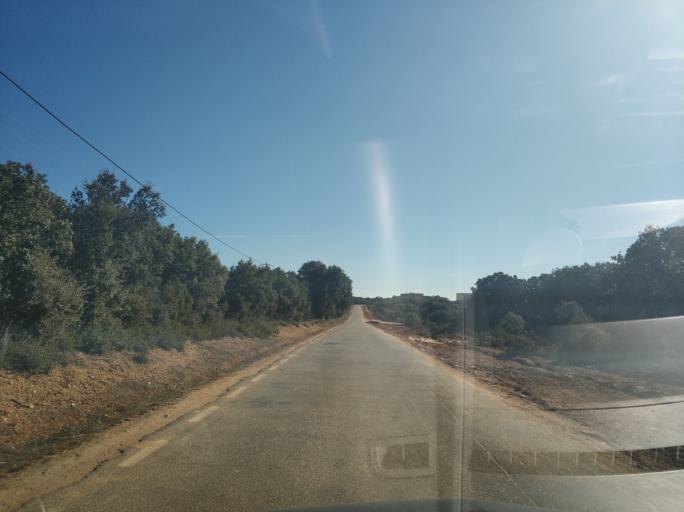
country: ES
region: Castille and Leon
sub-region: Provincia de Salamanca
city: Doninos de Salamanca
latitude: 40.9310
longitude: -5.7432
